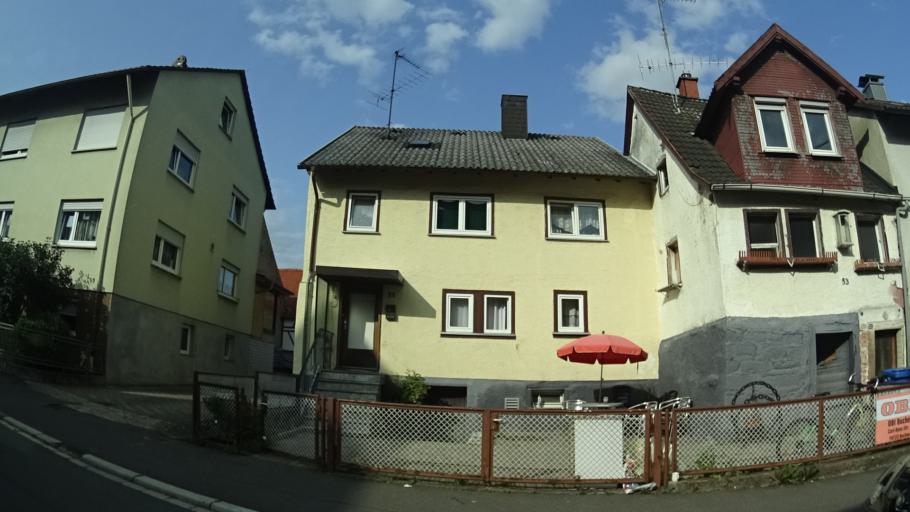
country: DE
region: Baden-Wuerttemberg
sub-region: Karlsruhe Region
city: Walldurn
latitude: 49.5815
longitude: 9.3713
